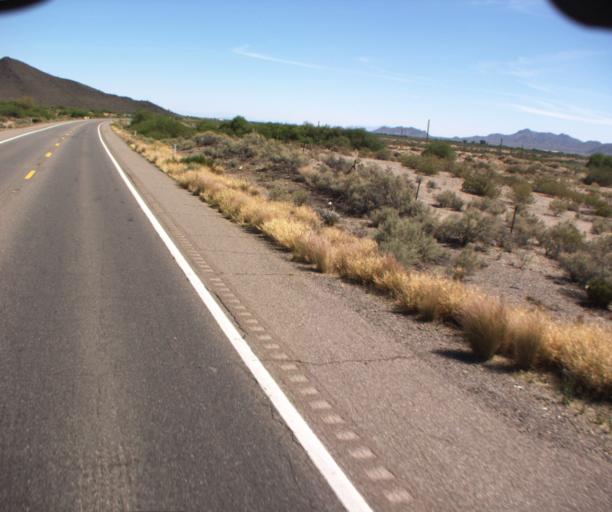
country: US
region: Arizona
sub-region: Pinal County
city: Sacaton
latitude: 33.1192
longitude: -111.7317
